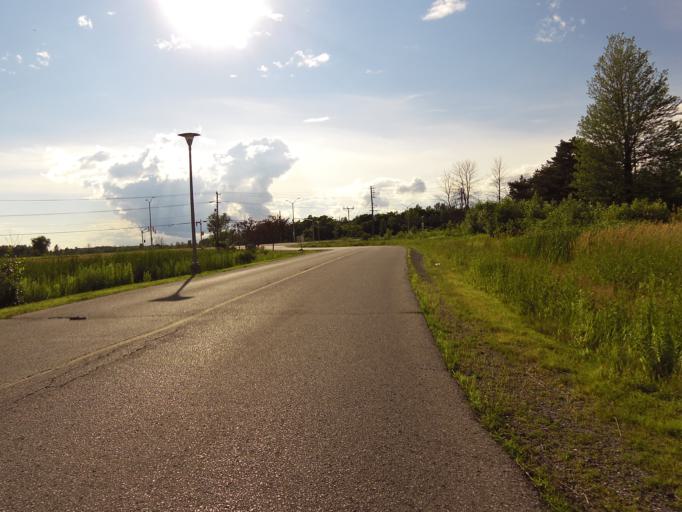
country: CA
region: Ontario
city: Bells Corners
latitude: 45.3456
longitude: -75.8419
